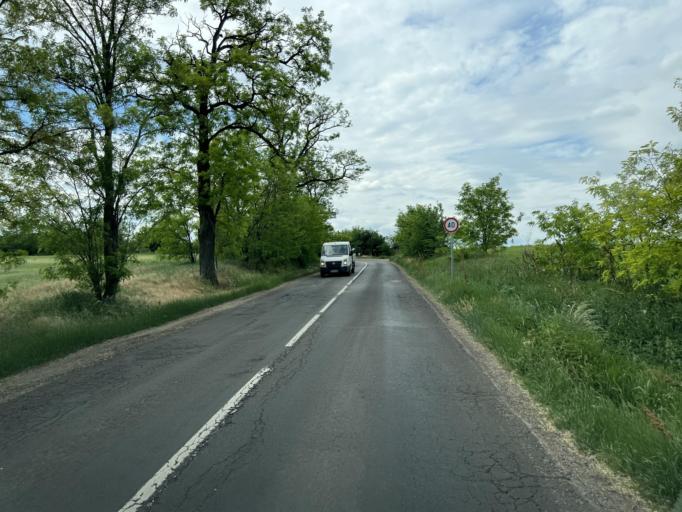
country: HU
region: Pest
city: Szentlorinckata
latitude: 47.4956
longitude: 19.7355
